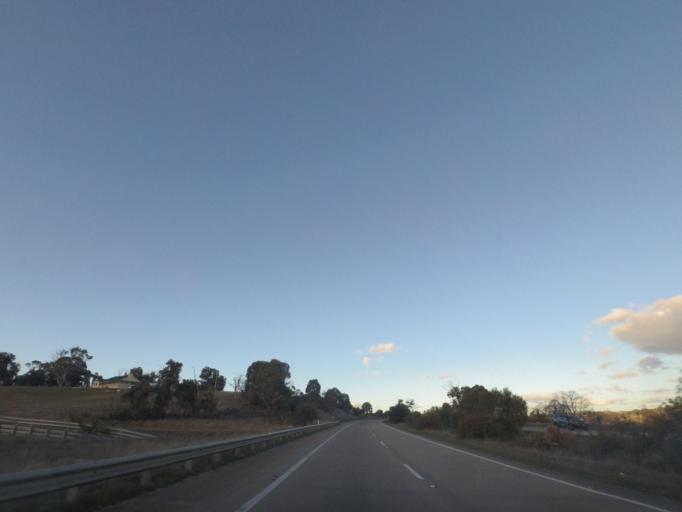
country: AU
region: New South Wales
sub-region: Yass Valley
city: Yass
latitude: -34.8048
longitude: 148.9103
